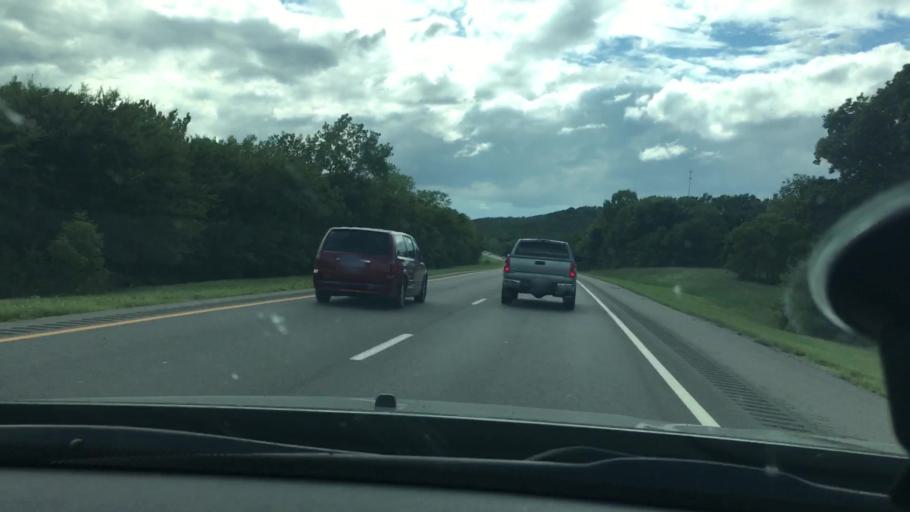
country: US
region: Oklahoma
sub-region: Okmulgee County
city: Morris
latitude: 35.4501
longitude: -95.7558
